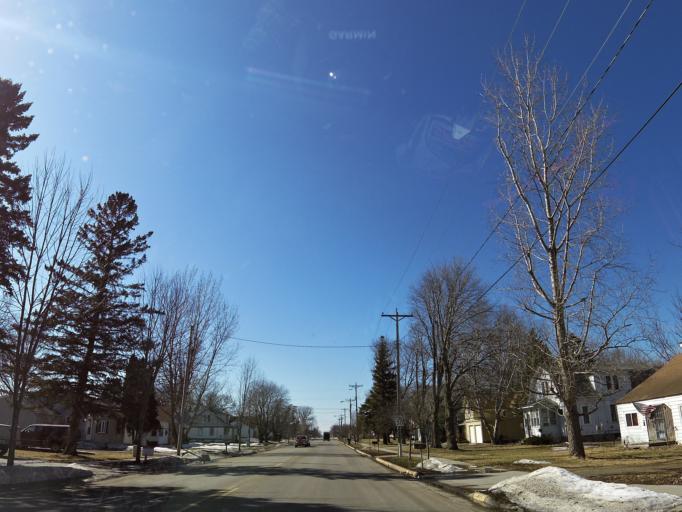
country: US
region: Minnesota
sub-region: Waseca County
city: New Richland
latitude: 43.8918
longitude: -93.4884
